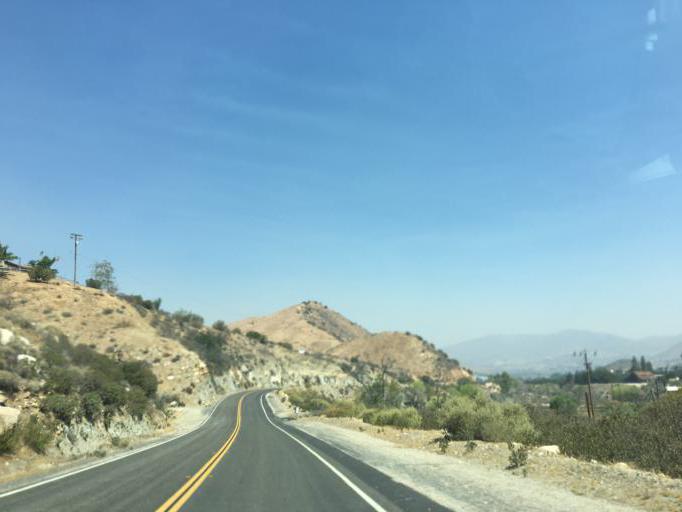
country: US
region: California
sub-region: Los Angeles County
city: Acton
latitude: 34.4558
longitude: -118.1566
